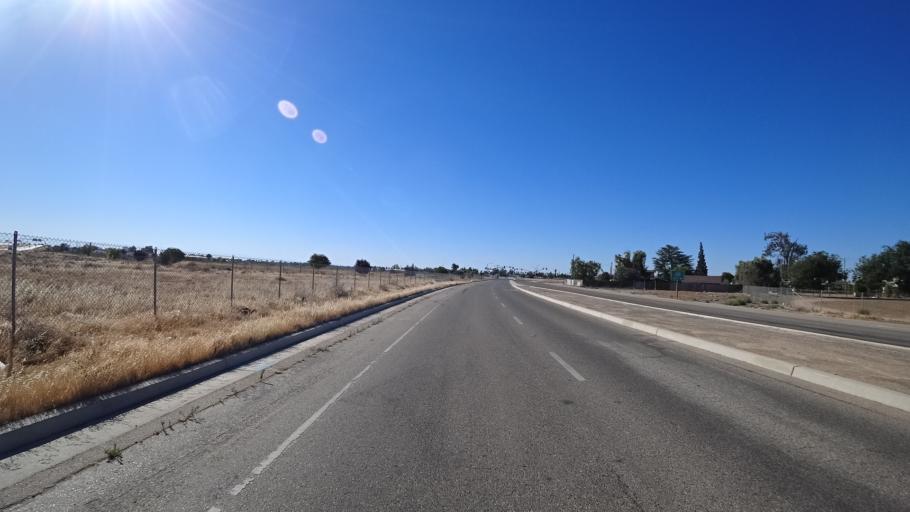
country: US
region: California
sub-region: Fresno County
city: West Park
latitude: 36.7374
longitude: -119.8309
